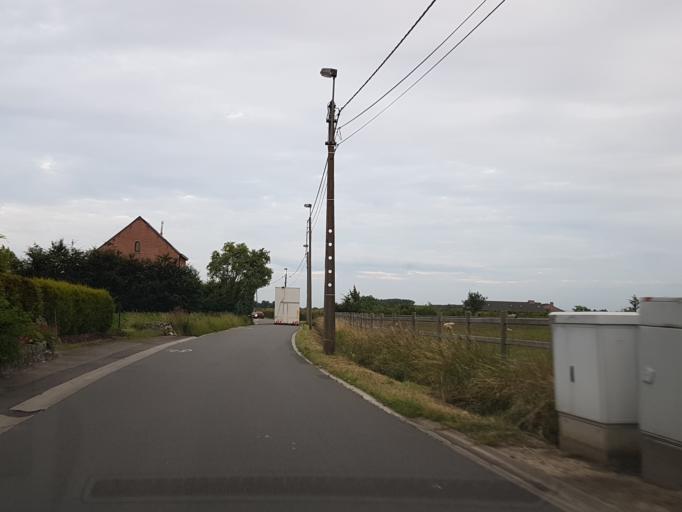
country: BE
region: Flanders
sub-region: Provincie Vlaams-Brabant
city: Kapelle-op-den-Bos
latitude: 50.9950
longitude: 4.3392
